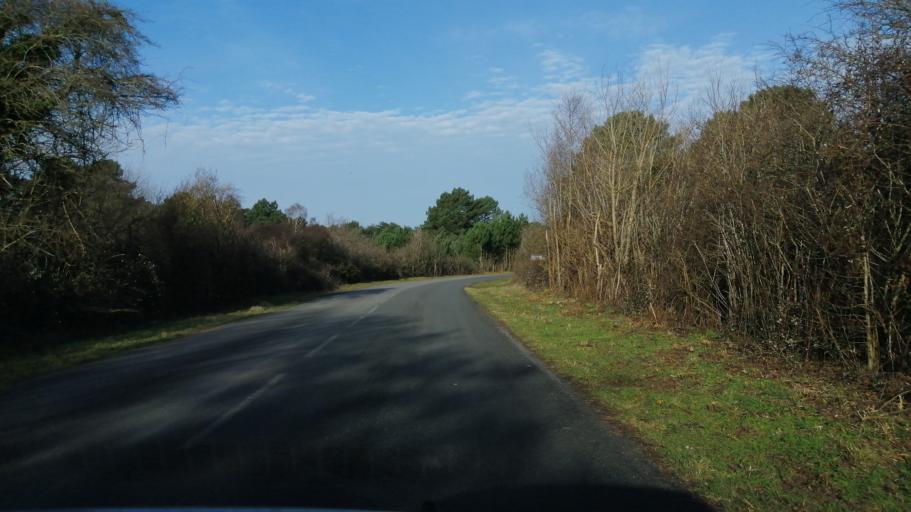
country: FR
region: Nord-Pas-de-Calais
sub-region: Departement du Pas-de-Calais
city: Dannes
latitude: 50.5908
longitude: 1.6046
